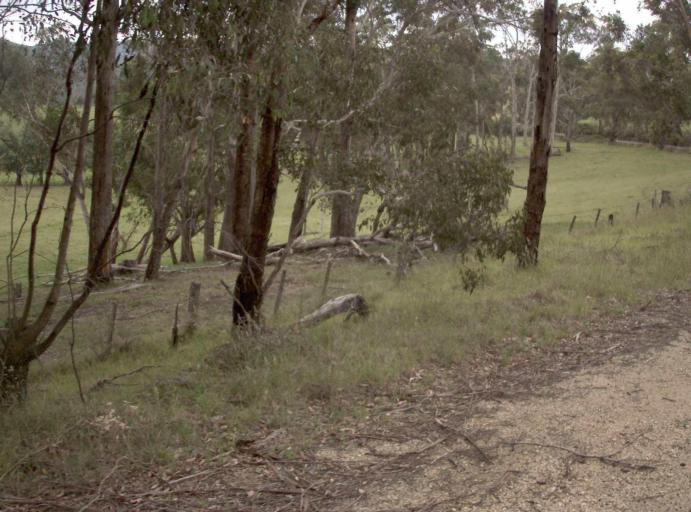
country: AU
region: New South Wales
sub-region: Bombala
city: Bombala
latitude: -37.4776
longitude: 149.1807
